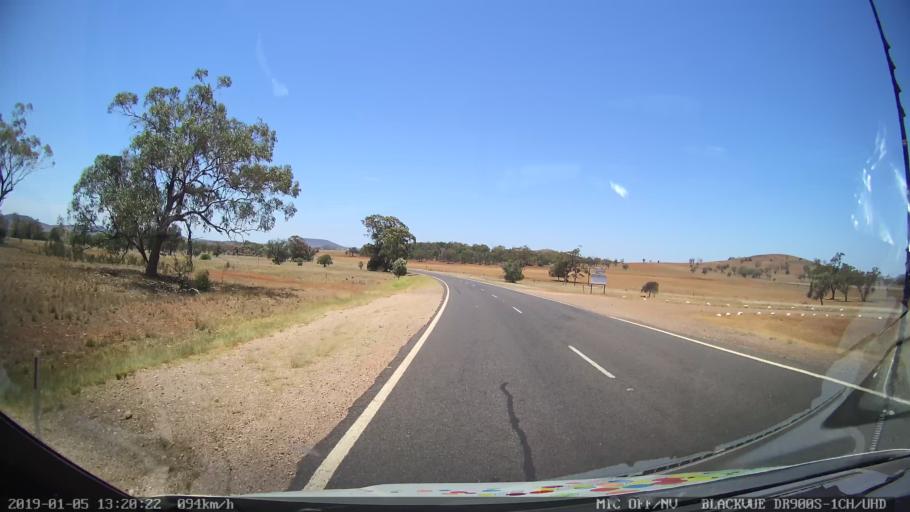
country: AU
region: New South Wales
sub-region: Gunnedah
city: Gunnedah
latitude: -31.1020
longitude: 149.9342
